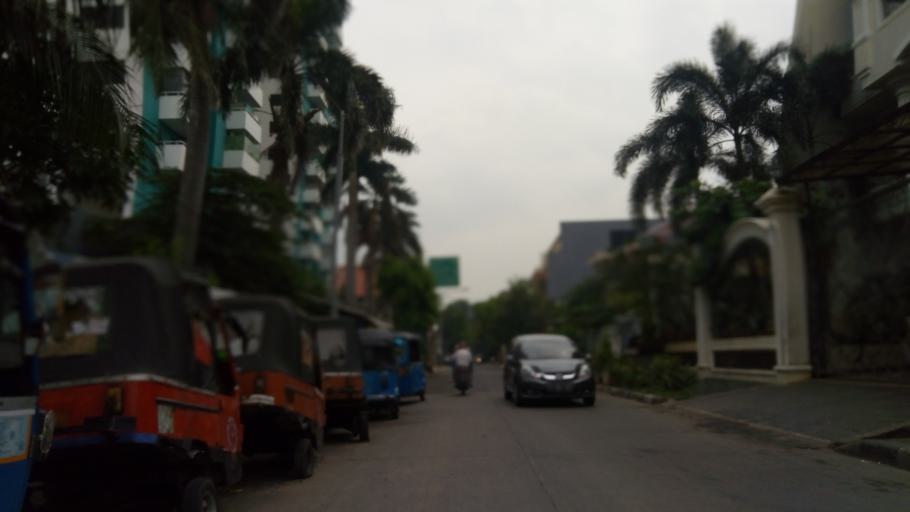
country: ID
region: Jakarta Raya
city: Jakarta
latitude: -6.1451
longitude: 106.8391
